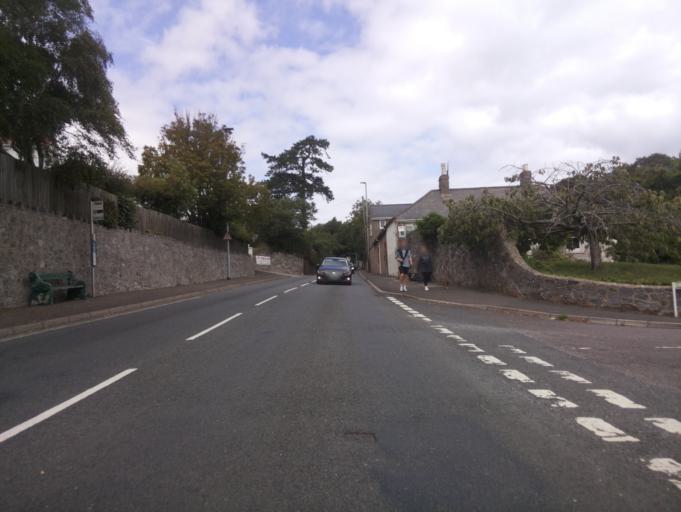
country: GB
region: England
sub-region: Devon
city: Teignmouth
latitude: 50.5512
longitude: -3.4923
